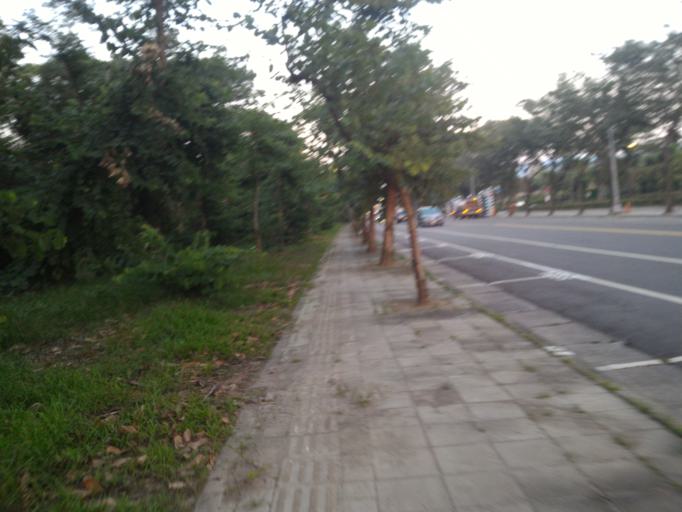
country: TW
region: Taiwan
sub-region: Taoyuan
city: Taoyuan
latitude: 24.9514
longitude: 121.3838
